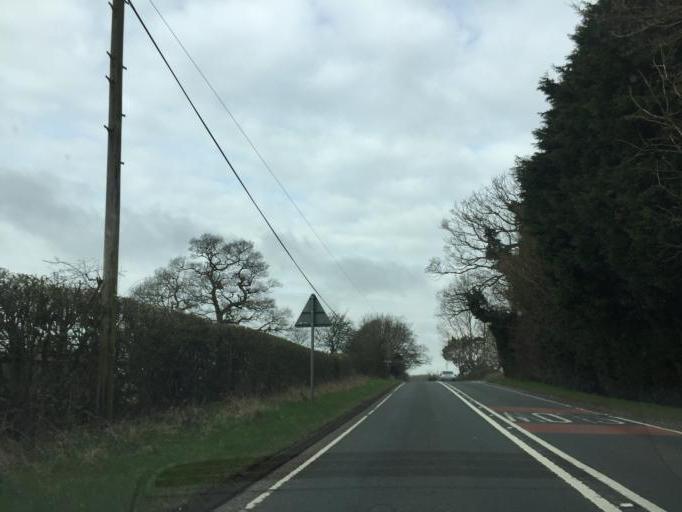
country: GB
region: England
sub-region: Warwickshire
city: Henley in Arden
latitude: 52.2989
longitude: -1.8295
